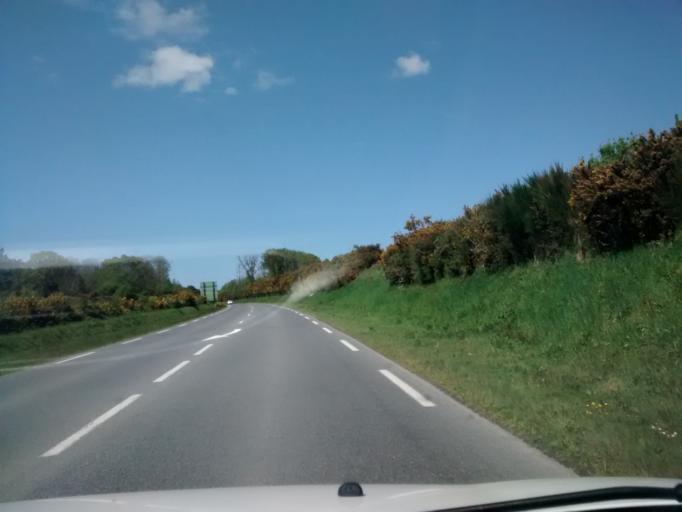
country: FR
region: Brittany
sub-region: Departement des Cotes-d'Armor
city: Pleslin-Trigavou
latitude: 48.5403
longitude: -2.0368
